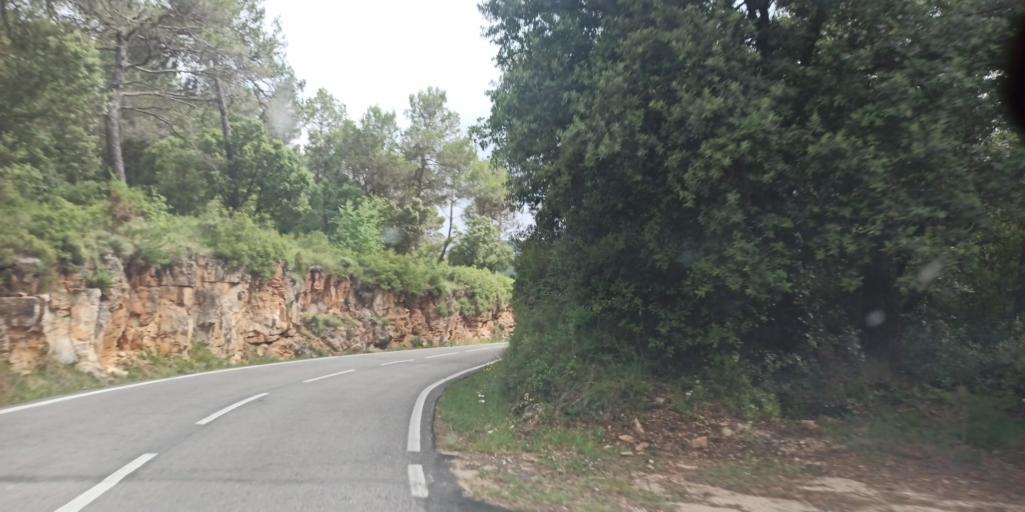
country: ES
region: Catalonia
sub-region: Provincia de Tarragona
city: Querol
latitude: 41.3949
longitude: 1.4710
